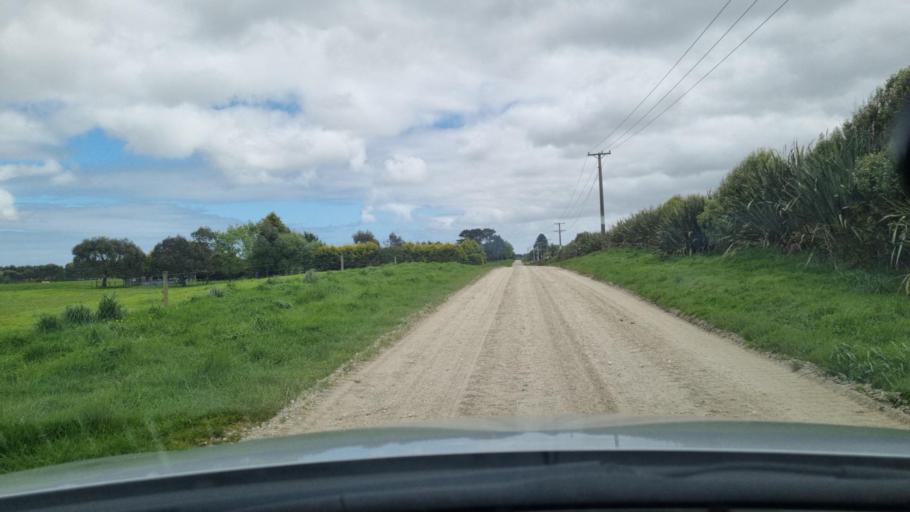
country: NZ
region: Southland
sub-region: Invercargill City
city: Invercargill
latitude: -46.4433
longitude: 168.4127
